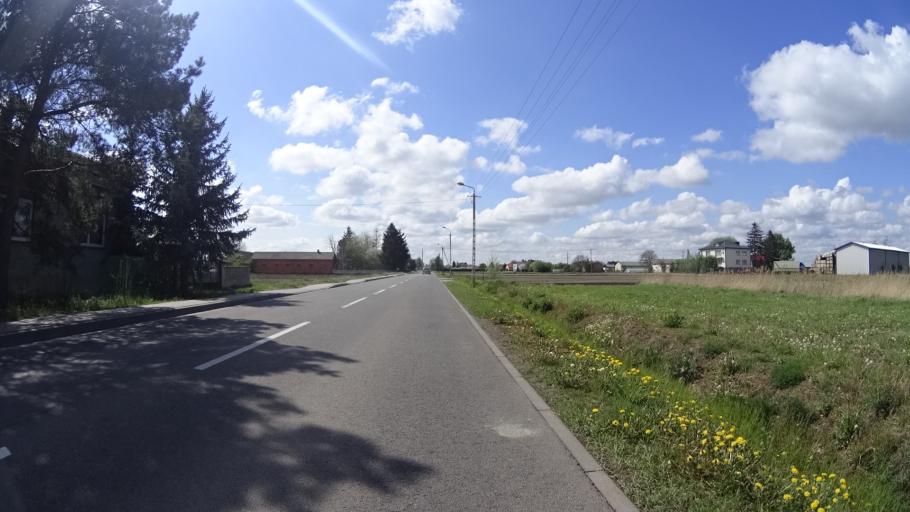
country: PL
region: Masovian Voivodeship
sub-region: Powiat warszawski zachodni
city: Ozarow Mazowiecki
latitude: 52.2307
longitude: 20.7540
